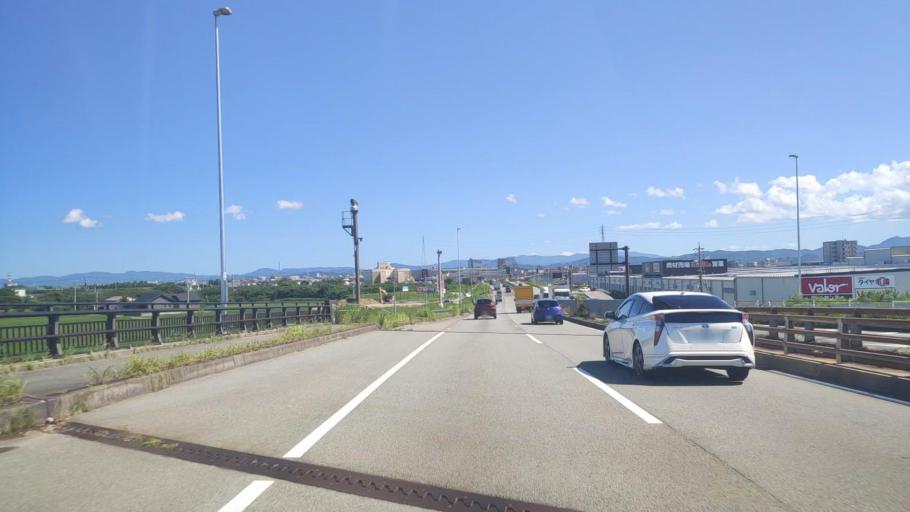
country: JP
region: Mie
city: Hisai-motomachi
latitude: 34.6111
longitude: 136.5187
